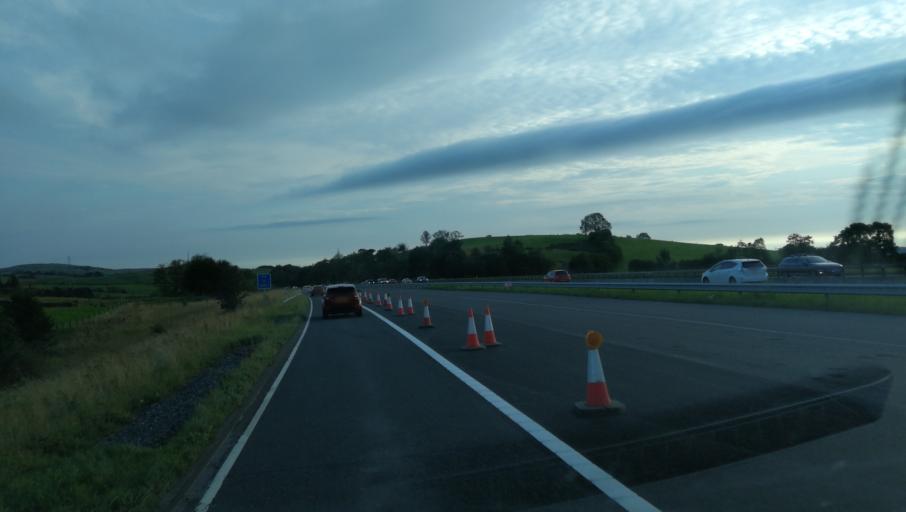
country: GB
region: England
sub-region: Cumbria
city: Kendal
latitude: 54.2998
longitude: -2.6504
